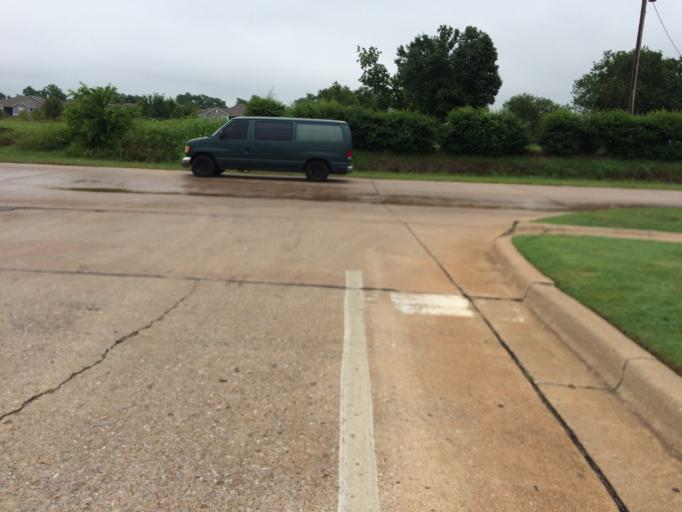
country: US
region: Oklahoma
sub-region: Cleveland County
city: Hall Park
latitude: 35.2075
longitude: -97.4063
